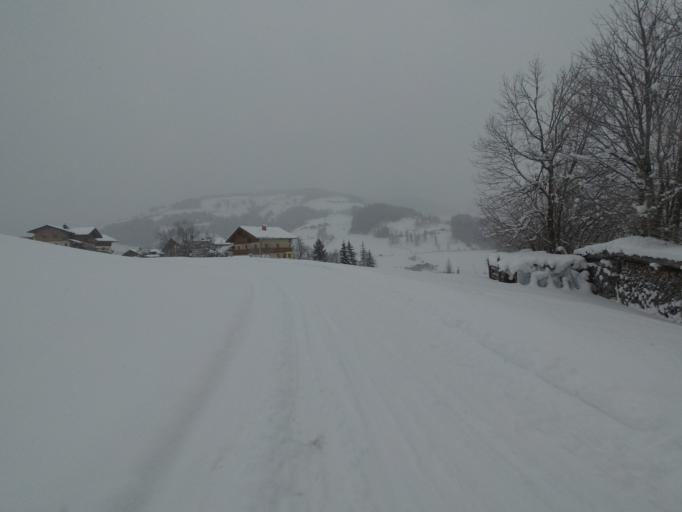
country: AT
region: Salzburg
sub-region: Politischer Bezirk Sankt Johann im Pongau
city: Wagrain
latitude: 47.3300
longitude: 13.2952
